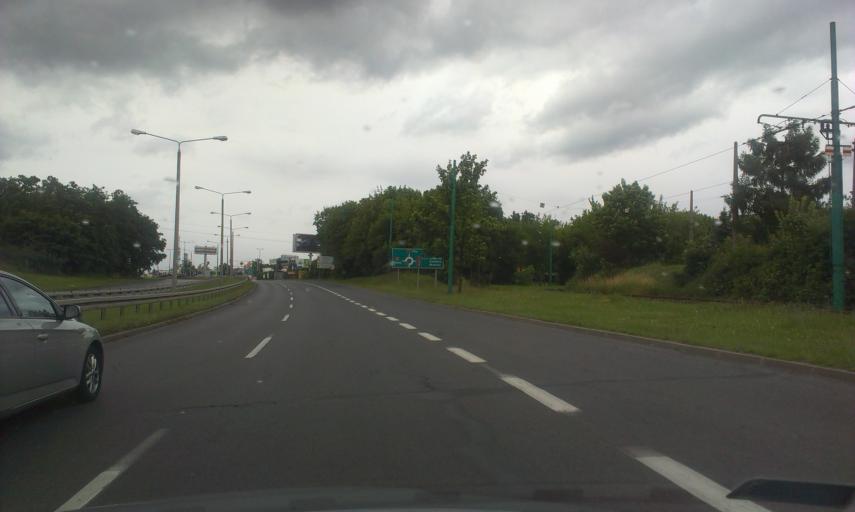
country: PL
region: Greater Poland Voivodeship
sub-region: Poznan
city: Poznan
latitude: 52.4402
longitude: 16.9100
